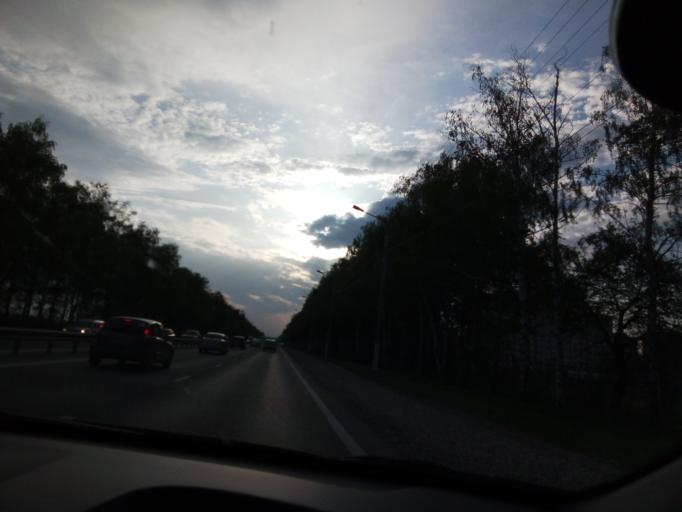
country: RU
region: Chuvashia
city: Novocheboksarsk
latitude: 56.1240
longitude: 47.3956
